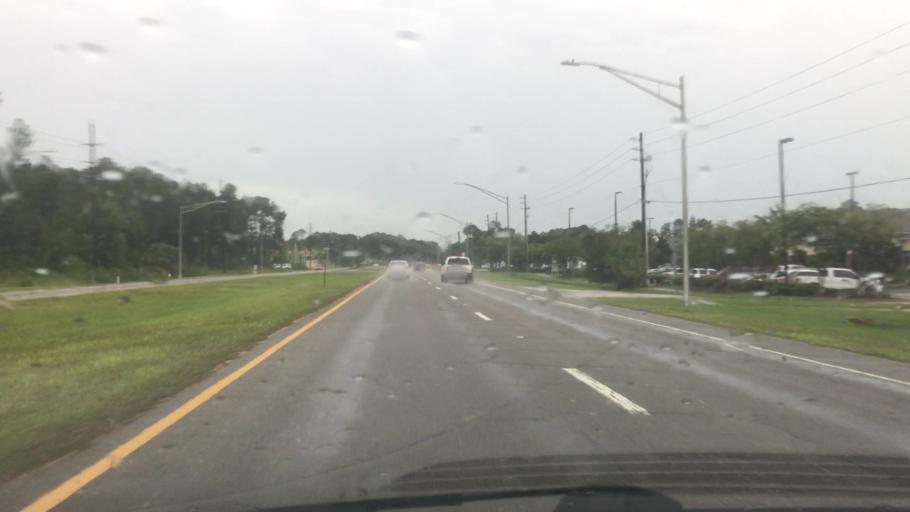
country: US
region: Florida
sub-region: Duval County
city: Neptune Beach
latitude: 30.3031
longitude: -81.5259
